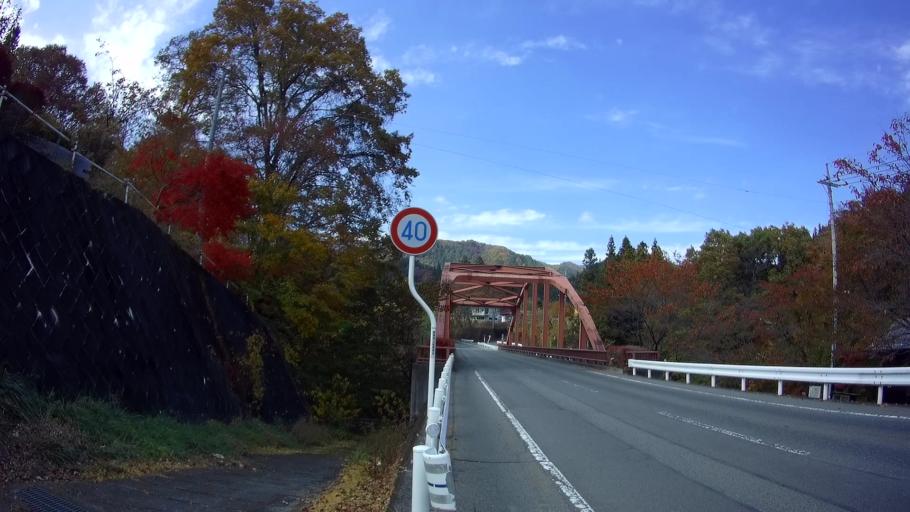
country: JP
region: Gunma
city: Nakanojomachi
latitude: 36.5066
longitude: 138.7139
